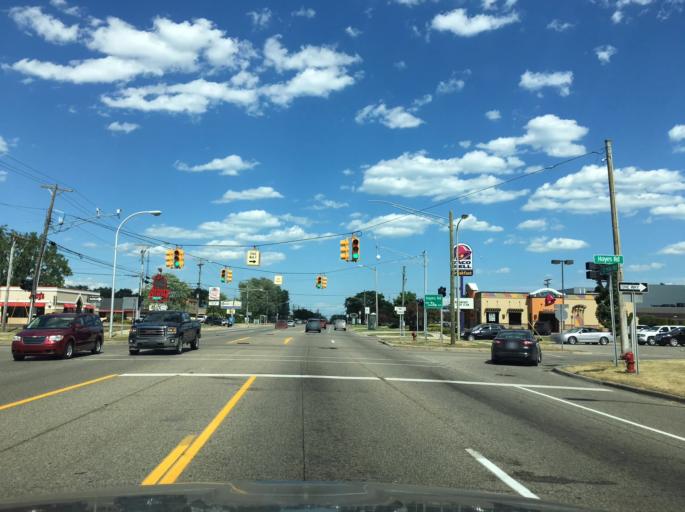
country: US
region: Michigan
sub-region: Macomb County
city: Roseville
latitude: 42.5088
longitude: -82.9690
